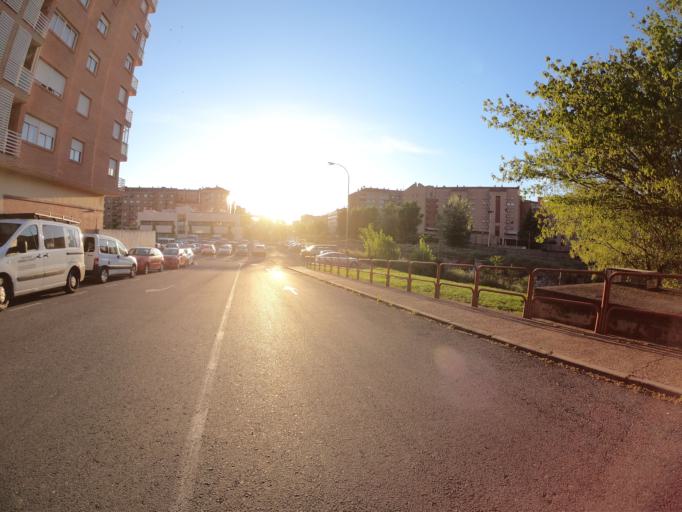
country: ES
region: La Rioja
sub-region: Provincia de La Rioja
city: Logrono
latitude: 42.4579
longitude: -2.4547
